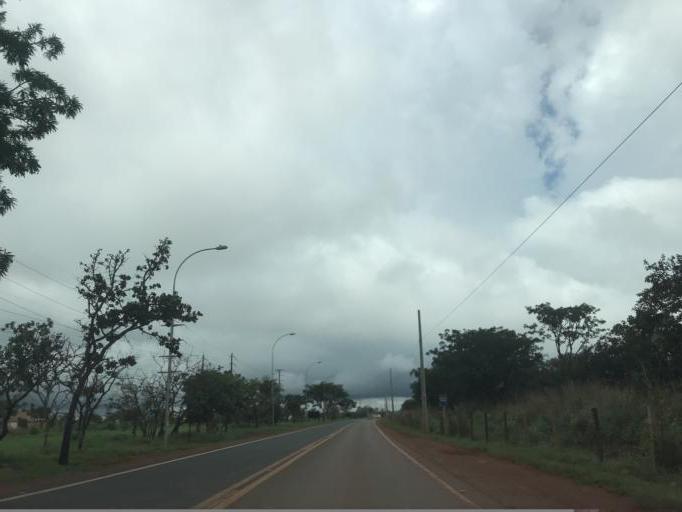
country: BR
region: Federal District
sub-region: Brasilia
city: Brasilia
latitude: -15.8239
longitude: -47.7957
